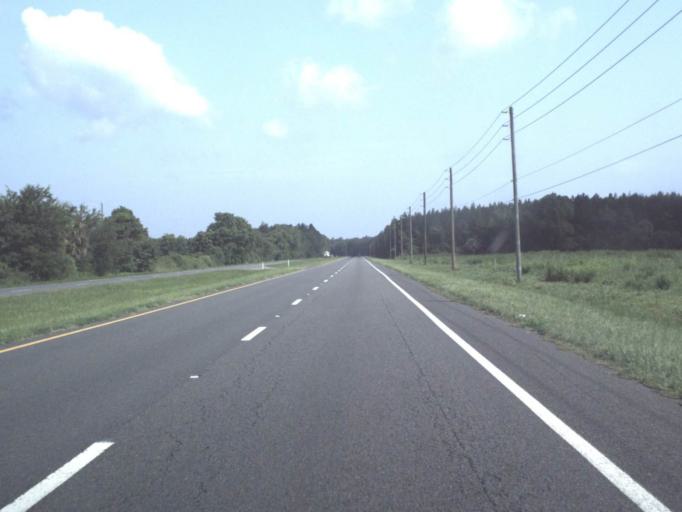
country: US
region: Florida
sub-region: Nassau County
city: Callahan
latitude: 30.6244
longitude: -81.8479
